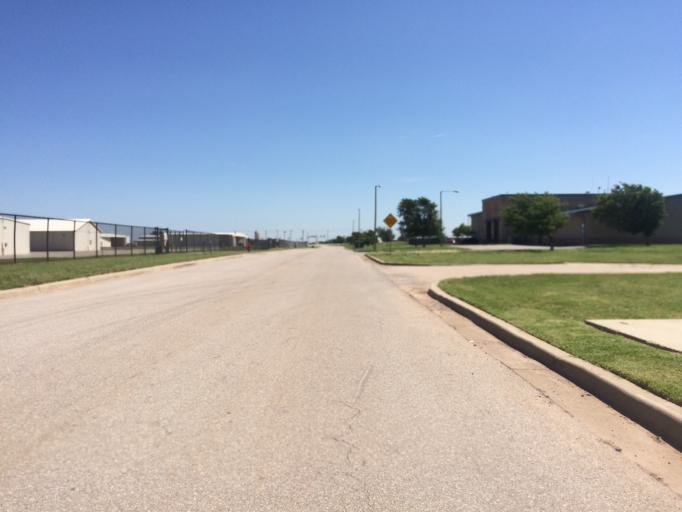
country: US
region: Oklahoma
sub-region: Cleveland County
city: Norman
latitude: 35.2439
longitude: -97.4638
